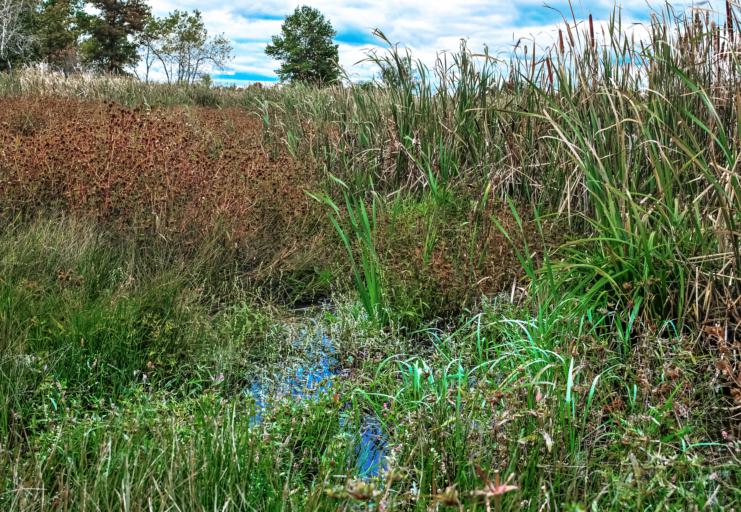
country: US
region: Wisconsin
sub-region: Jefferson County
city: Lake Mills
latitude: 43.1254
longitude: -88.9166
